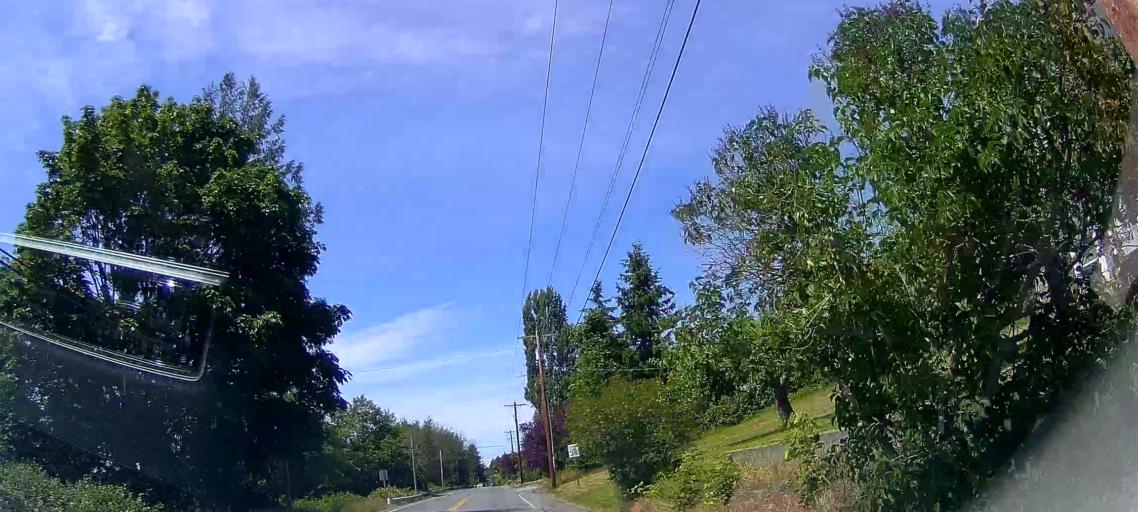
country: US
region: Washington
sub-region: Snohomish County
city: Stanwood
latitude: 48.2459
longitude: -122.3486
